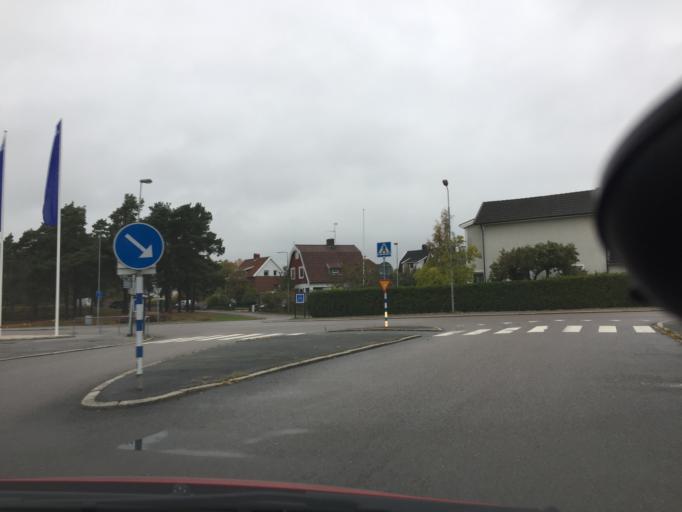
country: SE
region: Vaestra Goetaland
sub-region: Trollhattan
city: Trollhattan
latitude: 58.2893
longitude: 12.3002
